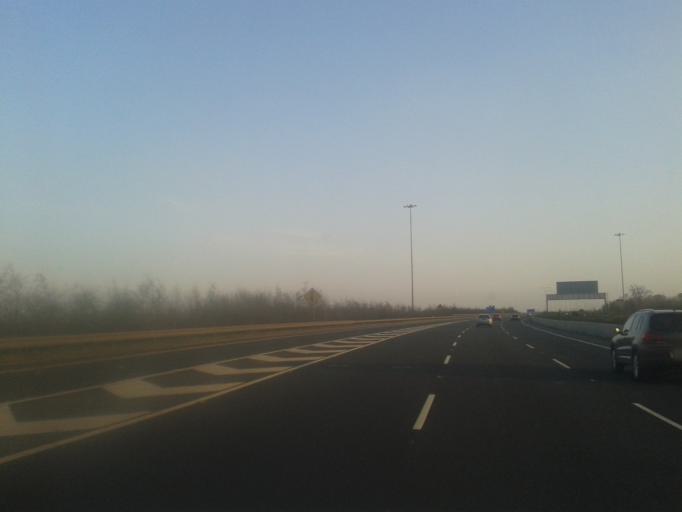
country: IE
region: Leinster
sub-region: Fingal County
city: Swords
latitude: 53.4722
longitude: -6.2026
